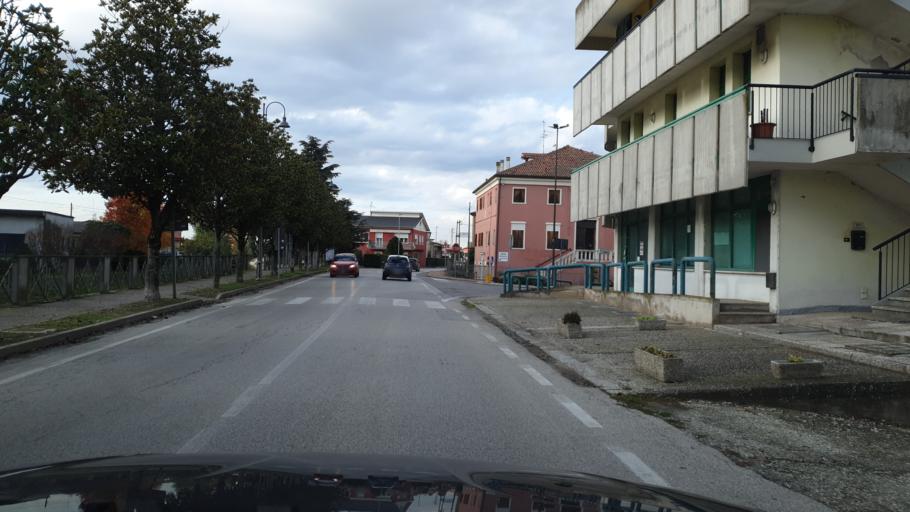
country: IT
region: Veneto
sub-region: Provincia di Rovigo
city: Villanova del Ghebbo Canton
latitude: 45.0568
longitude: 11.6436
